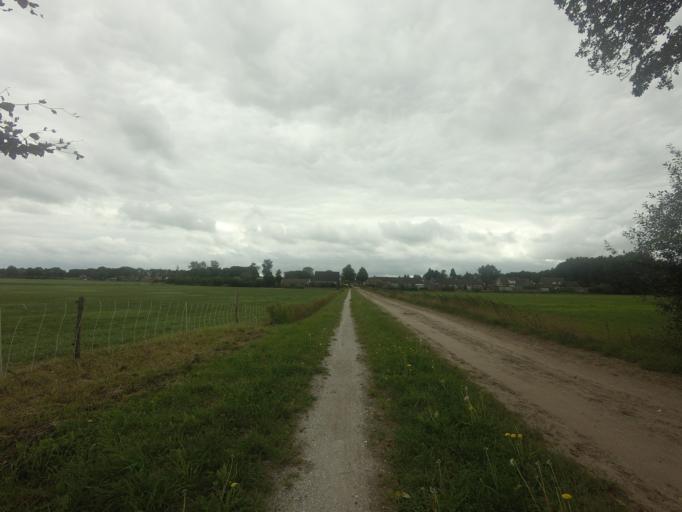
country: NL
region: Friesland
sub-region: Gemeente Weststellingwerf
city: Noordwolde
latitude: 52.9133
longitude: 6.1988
